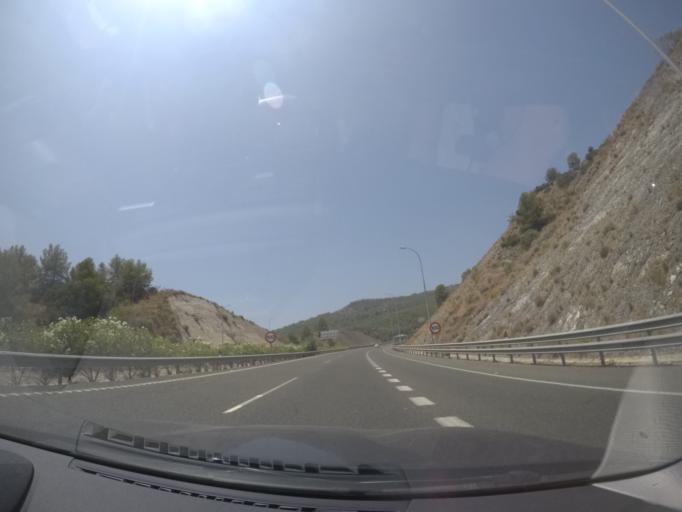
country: ES
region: Andalusia
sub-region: Provincia de Granada
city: La Herradura
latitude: 36.7501
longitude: -3.7558
